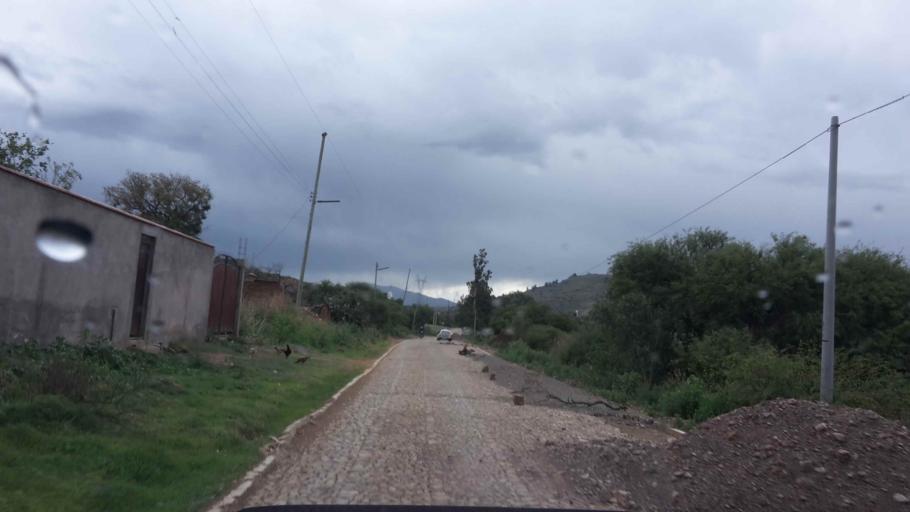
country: BO
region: Cochabamba
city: Cochabamba
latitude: -17.5465
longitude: -66.1864
